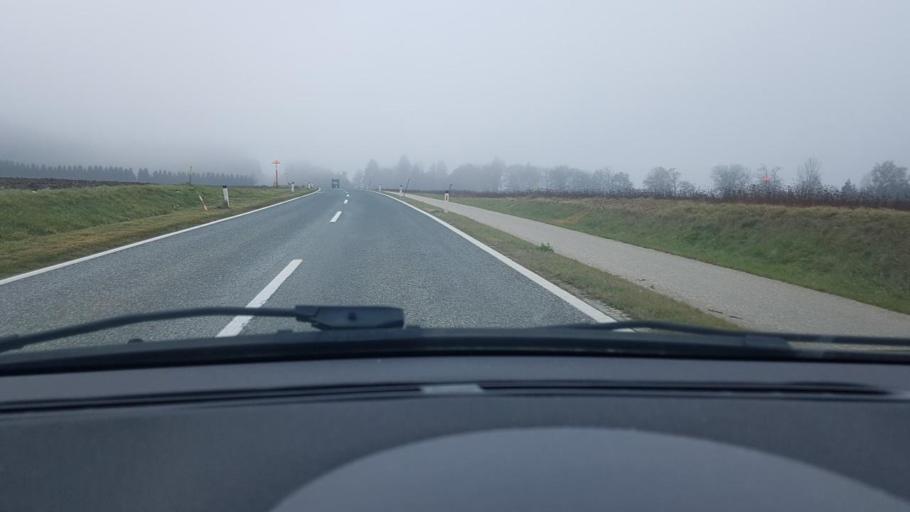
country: AT
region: Carinthia
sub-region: Politischer Bezirk Volkermarkt
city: Neuhaus
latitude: 46.6432
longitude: 14.8385
